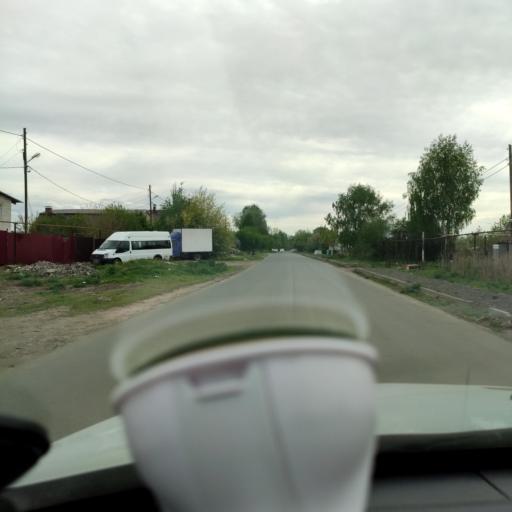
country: RU
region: Samara
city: Smyshlyayevka
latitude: 53.2192
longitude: 50.3349
